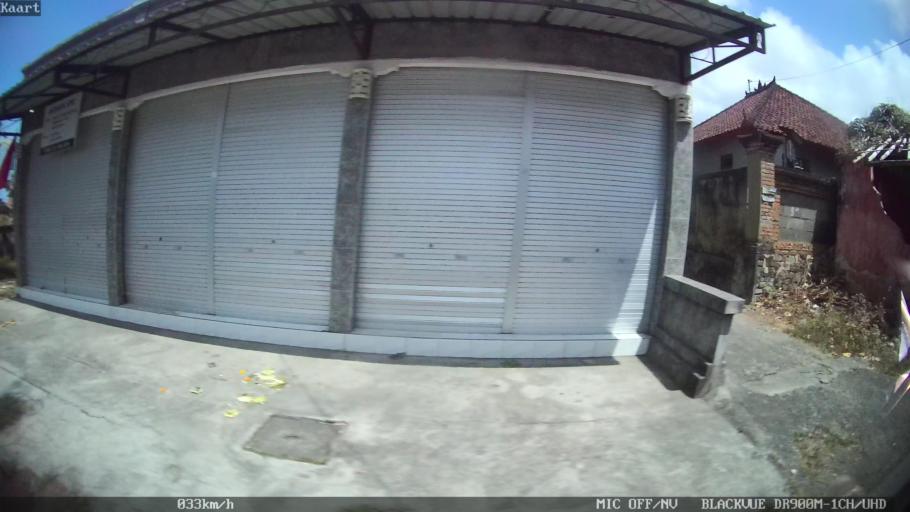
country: ID
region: Bali
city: Banjar Pasekan
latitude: -8.6010
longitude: 115.3090
